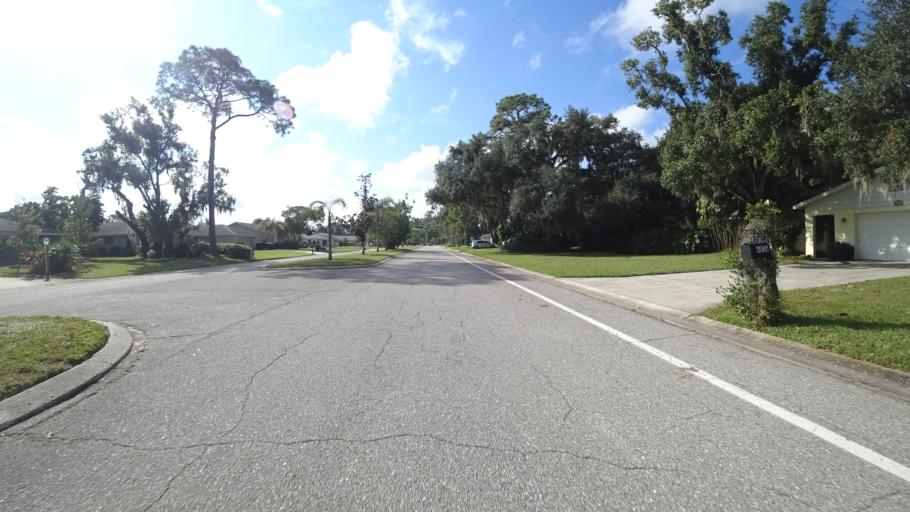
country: US
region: Florida
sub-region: Sarasota County
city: Desoto Lakes
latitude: 27.4024
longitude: -82.5009
